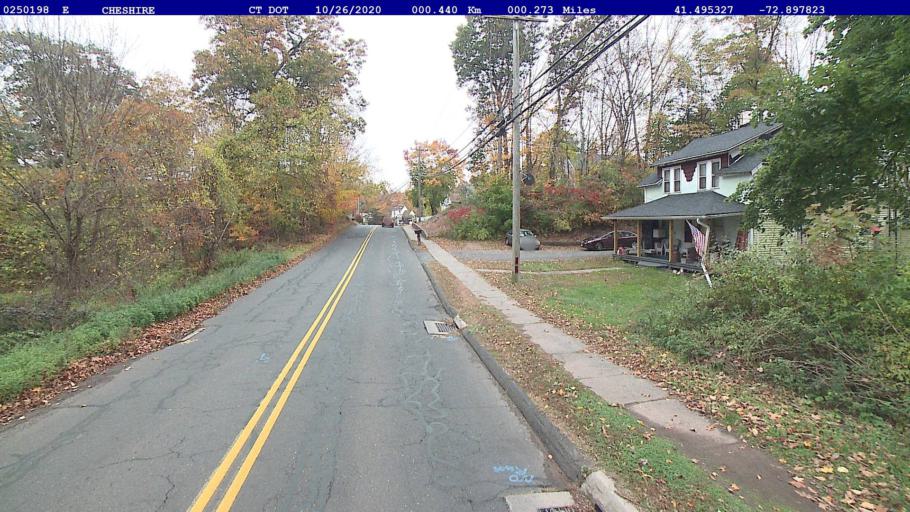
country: US
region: Connecticut
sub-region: New Haven County
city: Cheshire
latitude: 41.4953
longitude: -72.8978
